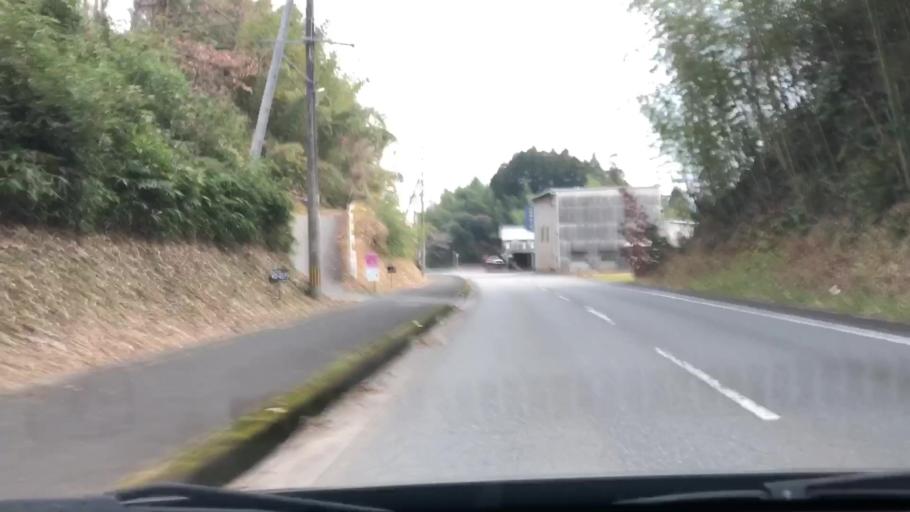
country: JP
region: Oita
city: Takedamachi
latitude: 32.9708
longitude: 131.5748
